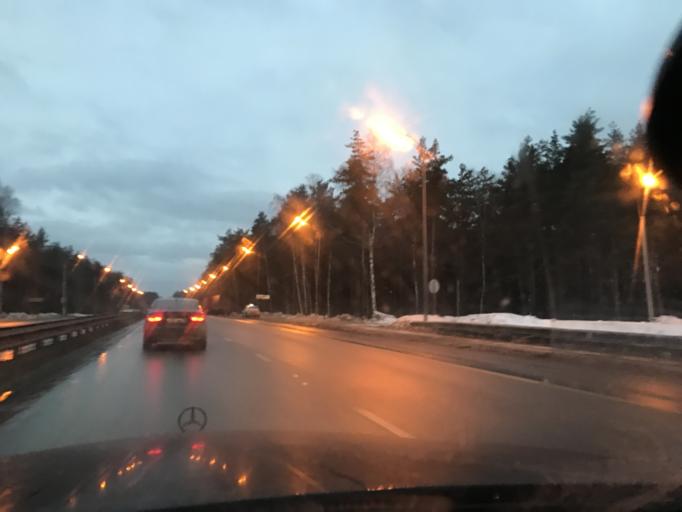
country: RU
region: Vladimir
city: Petushki
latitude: 55.9323
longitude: 39.3858
